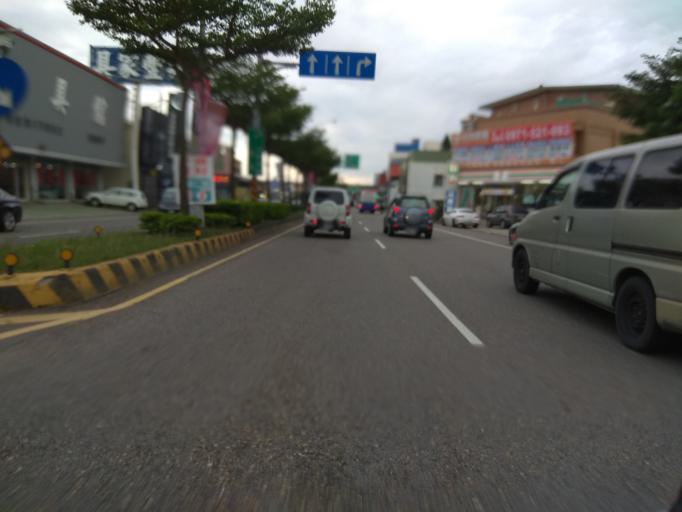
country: TW
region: Taiwan
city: Daxi
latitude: 24.9302
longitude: 121.2140
